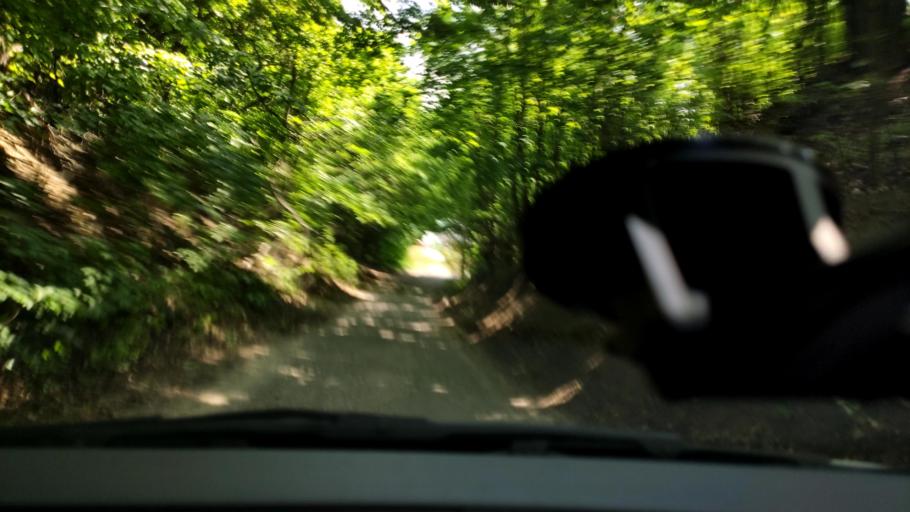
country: RU
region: Voronezj
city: Ramon'
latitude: 51.8976
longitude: 39.3375
